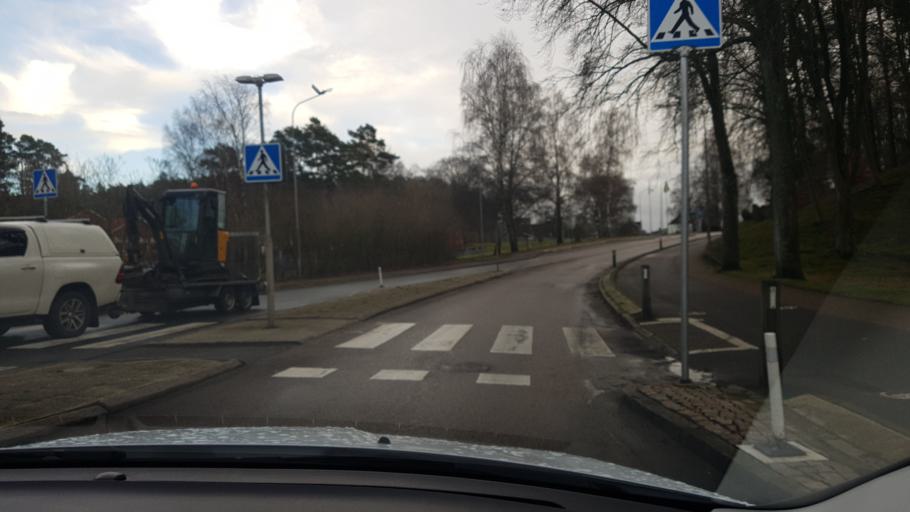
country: SE
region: Skane
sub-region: Hassleholms Kommun
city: Hassleholm
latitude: 56.1558
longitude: 13.7778
